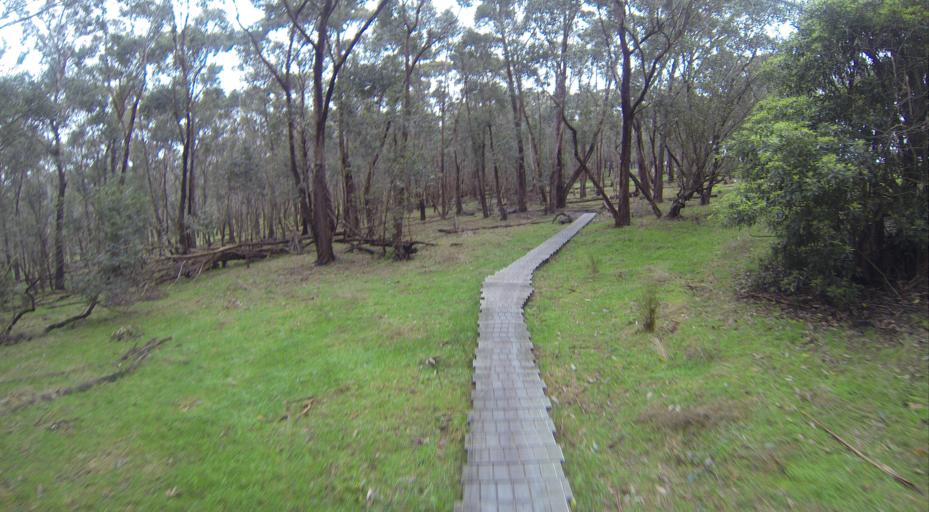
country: AU
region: Victoria
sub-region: Yarra Ranges
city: Lysterfield
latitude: -37.9592
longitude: 145.2894
